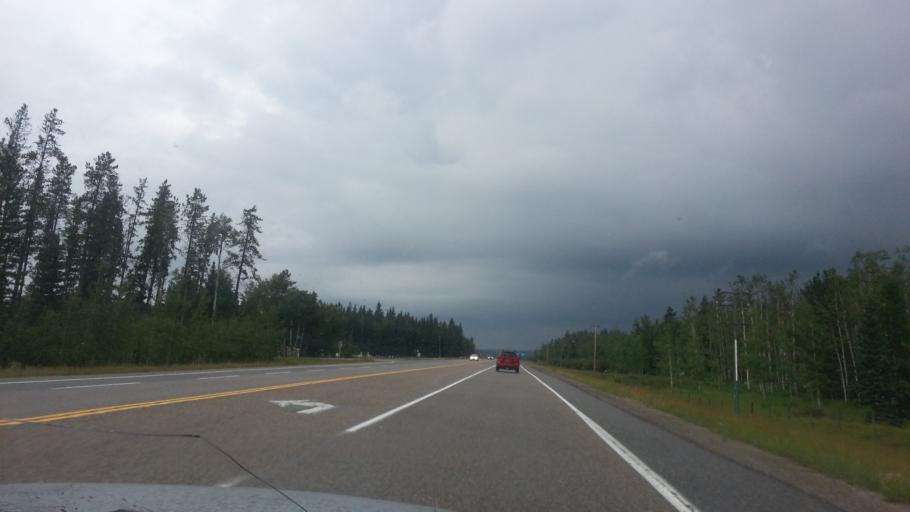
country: CA
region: Alberta
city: Cochrane
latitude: 50.9344
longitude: -114.5600
